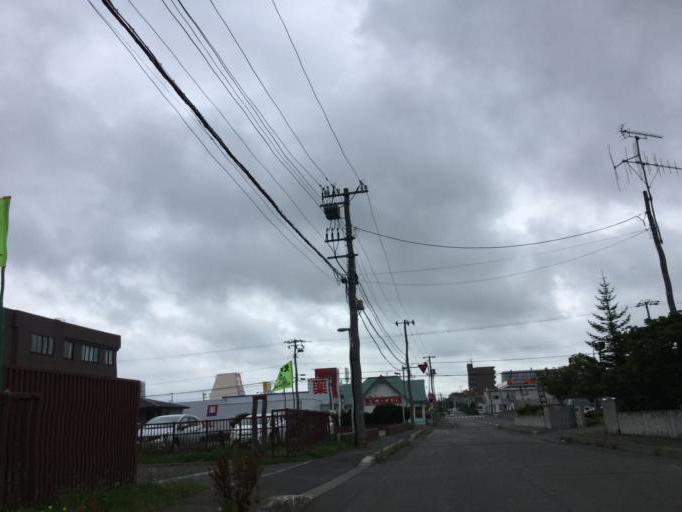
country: JP
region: Hokkaido
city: Wakkanai
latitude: 45.3978
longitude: 141.6991
